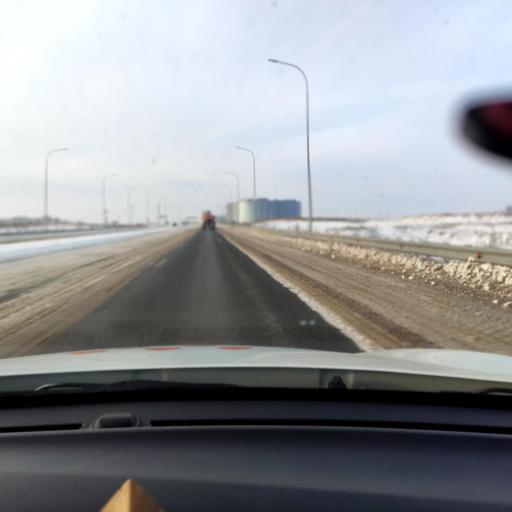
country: RU
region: Tatarstan
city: Sviyazhsk
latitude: 55.7479
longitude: 48.7622
